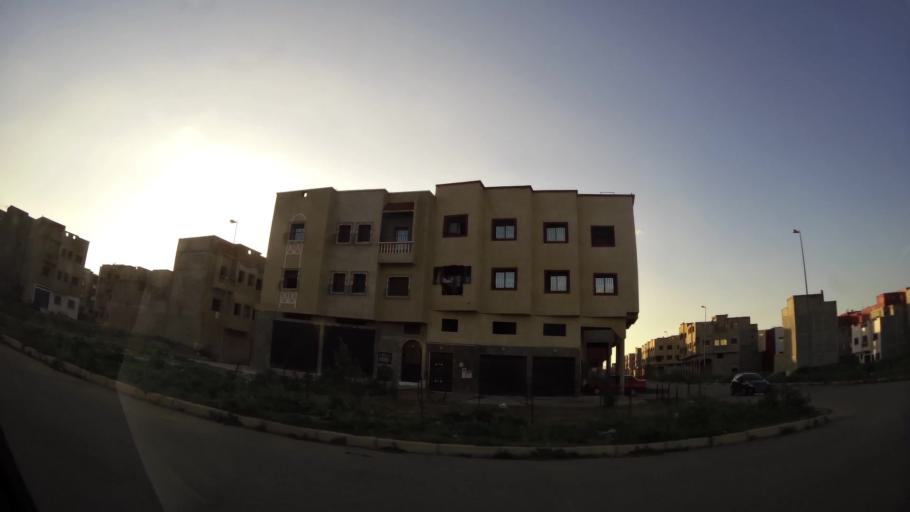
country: MA
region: Chaouia-Ouardigha
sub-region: Settat Province
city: Settat
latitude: 32.9846
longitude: -7.5970
